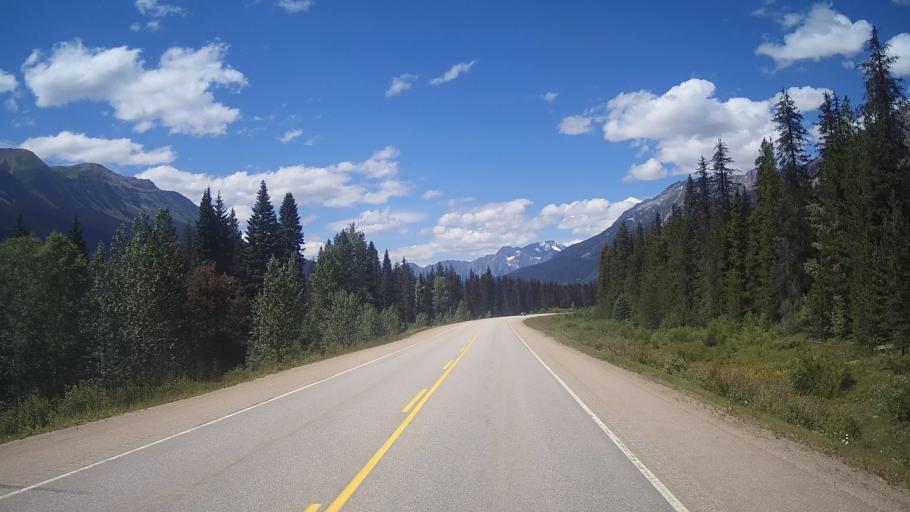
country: CA
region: Alberta
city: Grande Cache
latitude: 52.9902
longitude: -119.0093
